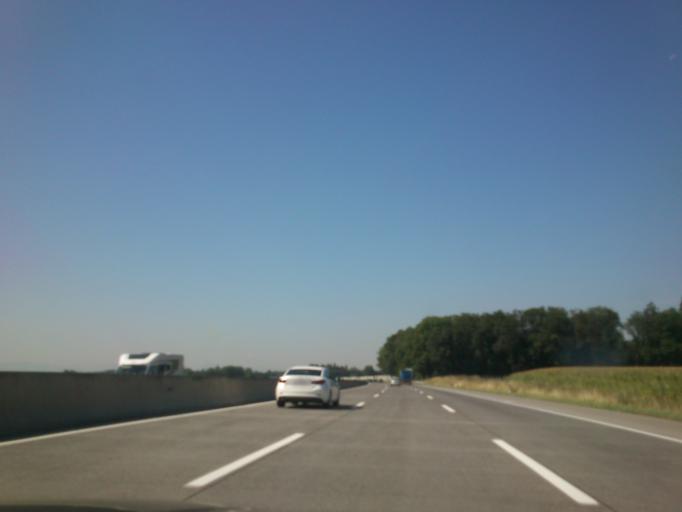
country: AT
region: Upper Austria
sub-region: Politischer Bezirk Linz-Land
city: Horsching
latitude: 48.1778
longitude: 14.1817
